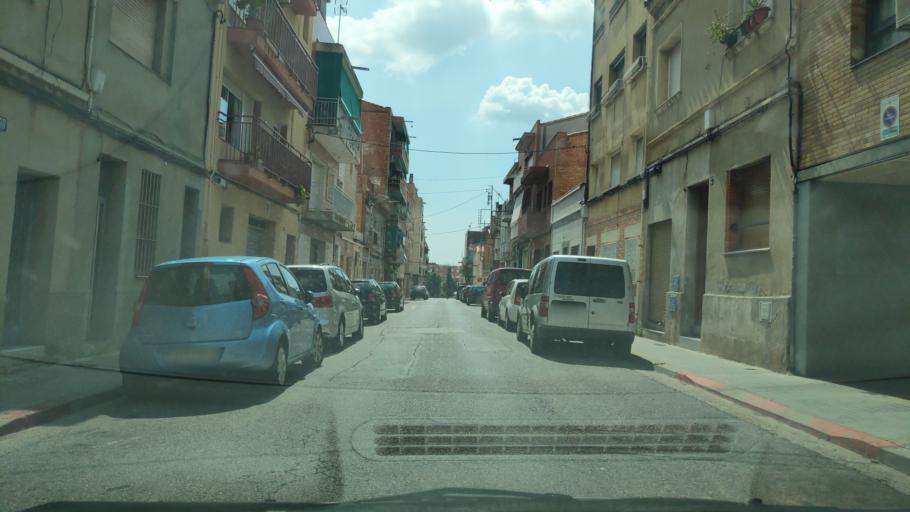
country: ES
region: Catalonia
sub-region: Provincia de Barcelona
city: Sant Quirze del Valles
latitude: 41.5493
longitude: 2.0881
